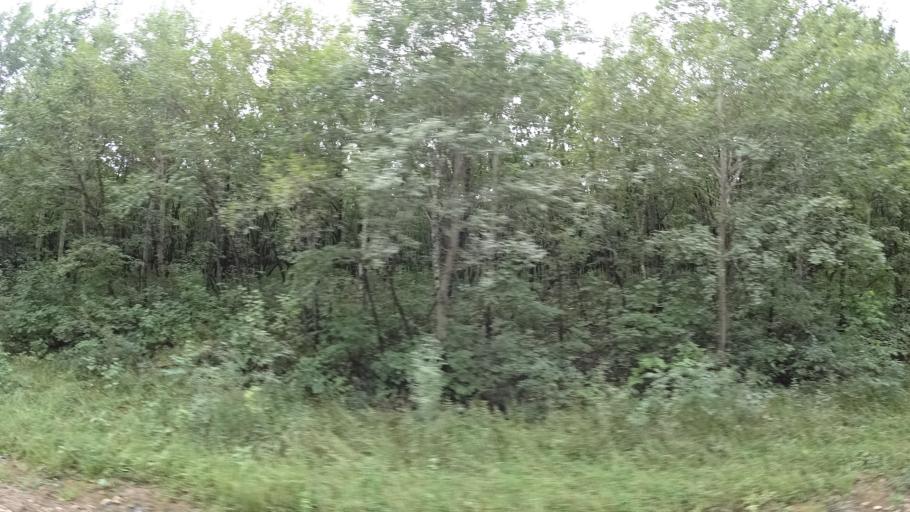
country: RU
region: Primorskiy
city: Lyalichi
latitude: 44.0845
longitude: 132.4432
